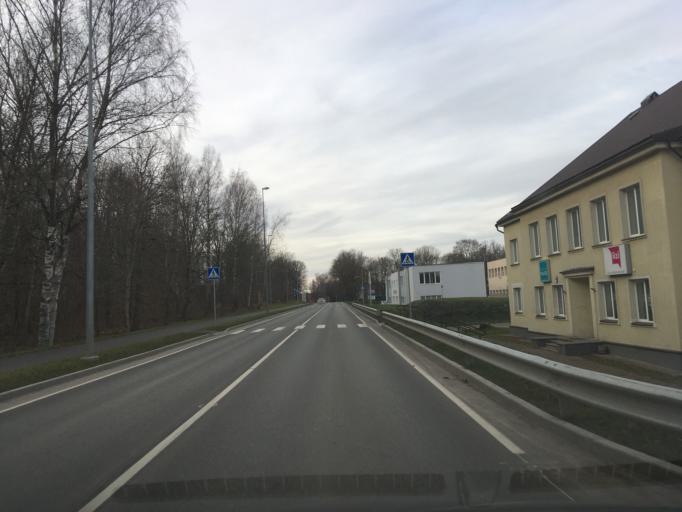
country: EE
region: Ida-Virumaa
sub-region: Johvi vald
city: Johvi
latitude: 59.3534
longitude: 27.4280
